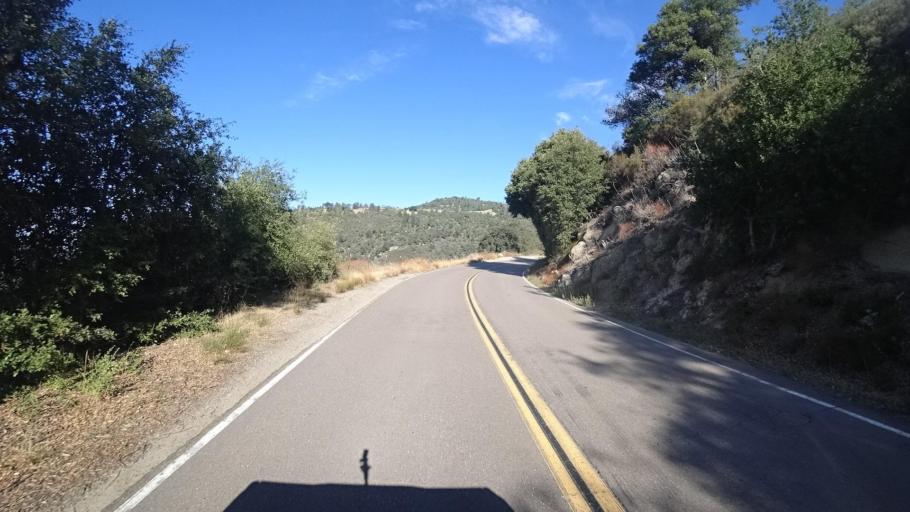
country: US
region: California
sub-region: Riverside County
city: Aguanga
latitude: 33.2739
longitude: -116.7831
